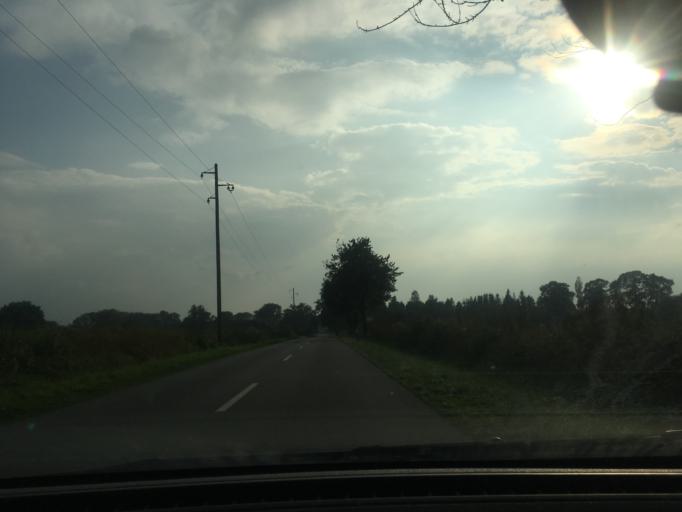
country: DE
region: Lower Saxony
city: Vastorf
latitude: 53.2088
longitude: 10.5485
